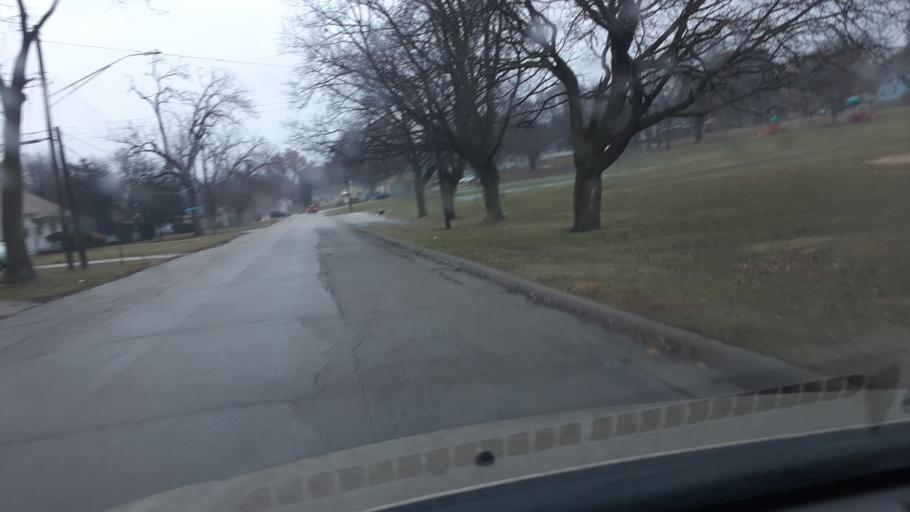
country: US
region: Illinois
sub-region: Winnebago County
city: Rockford
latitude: 42.2853
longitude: -89.1183
